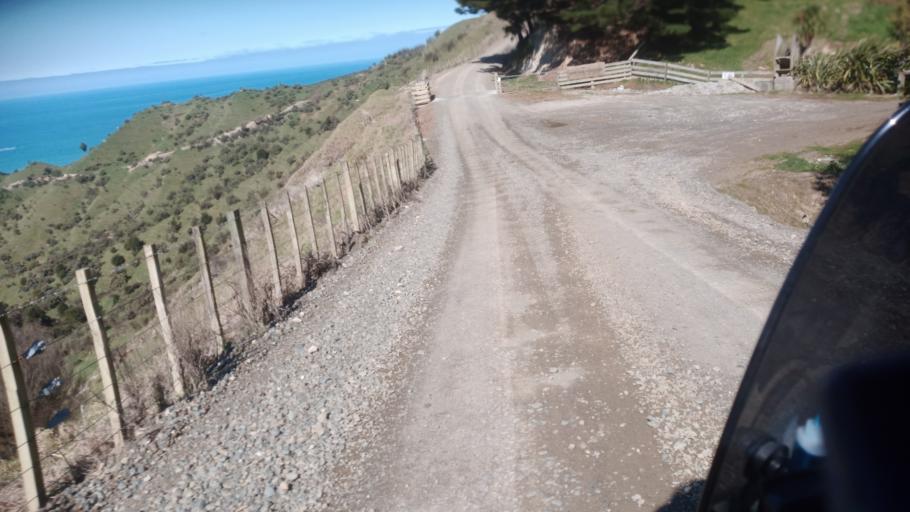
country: NZ
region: Gisborne
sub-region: Gisborne District
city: Gisborne
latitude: -39.1747
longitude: 177.9045
